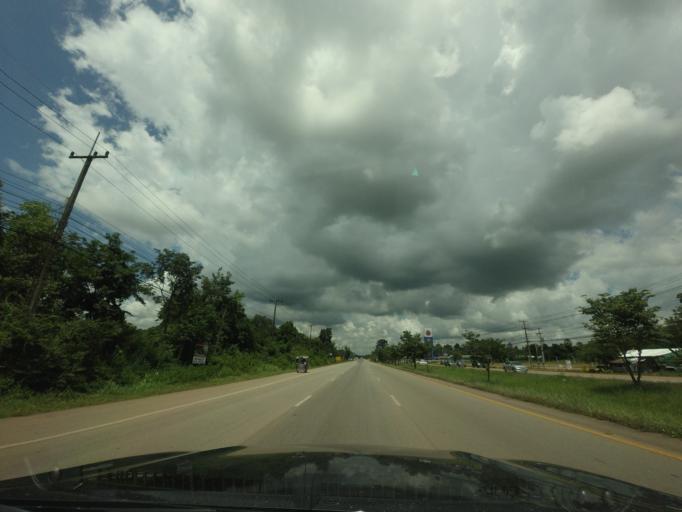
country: TH
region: Changwat Udon Thani
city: Udon Thani
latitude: 17.5412
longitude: 102.8002
